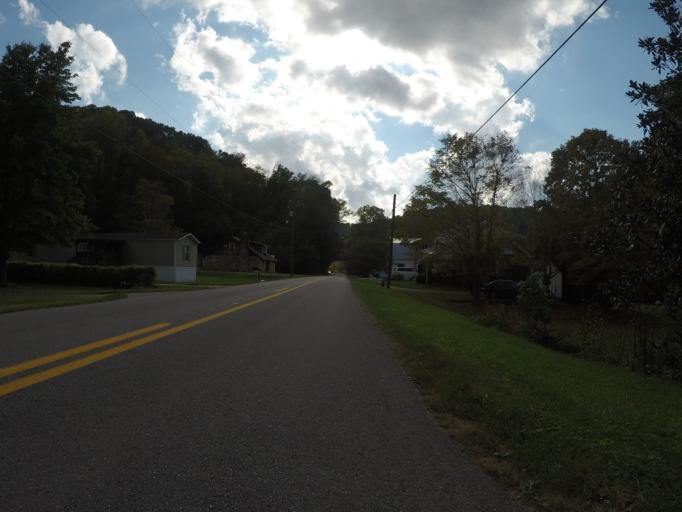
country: US
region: West Virginia
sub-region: Wayne County
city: Lavalette
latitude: 38.3492
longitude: -82.4484
